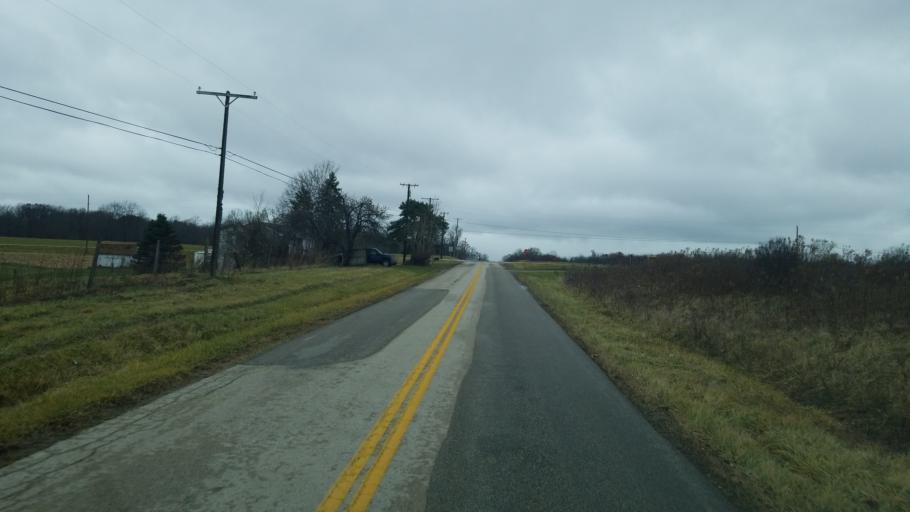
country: US
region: Ohio
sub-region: Ashtabula County
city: North Kingsville
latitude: 41.8616
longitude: -80.6175
